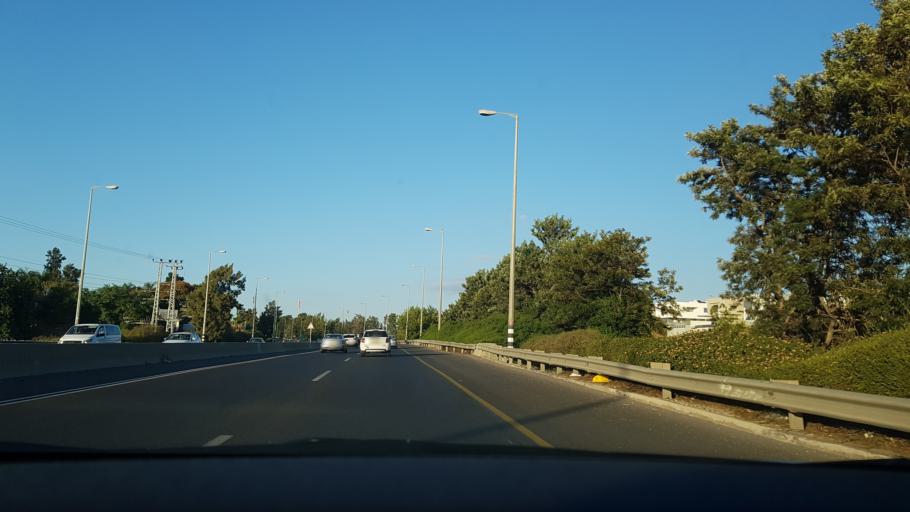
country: IL
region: Central District
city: Ness Ziona
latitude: 31.9314
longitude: 34.7757
